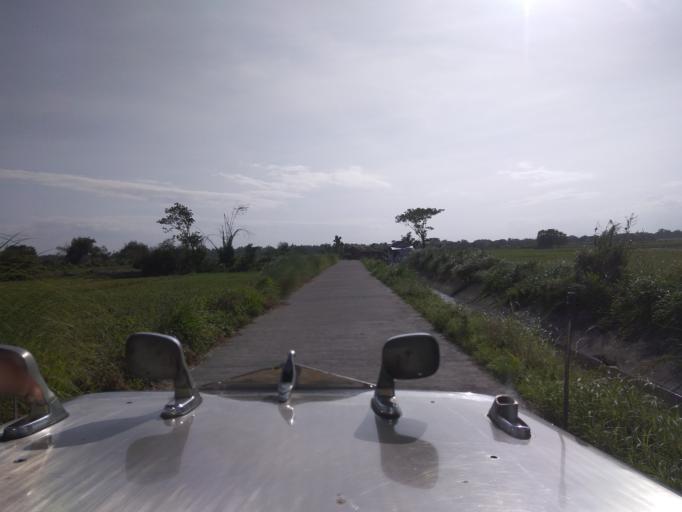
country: PH
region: Central Luzon
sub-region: Province of Pampanga
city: San Patricio
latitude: 15.1007
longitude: 120.7012
